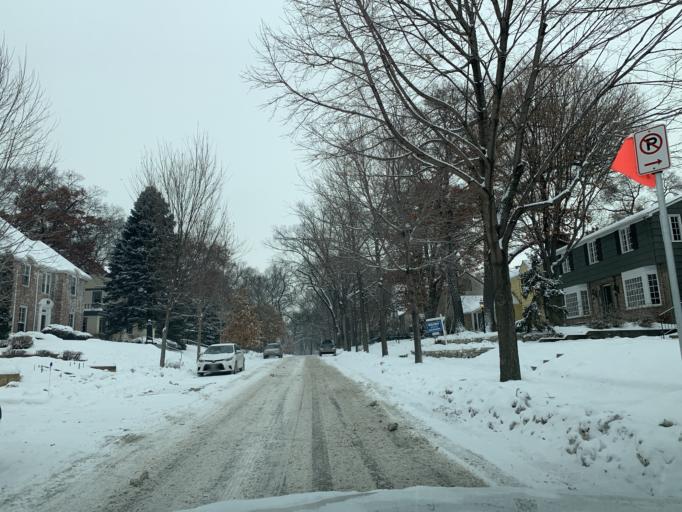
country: US
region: Minnesota
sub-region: Hennepin County
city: Saint Louis Park
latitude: 44.9487
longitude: -93.3263
